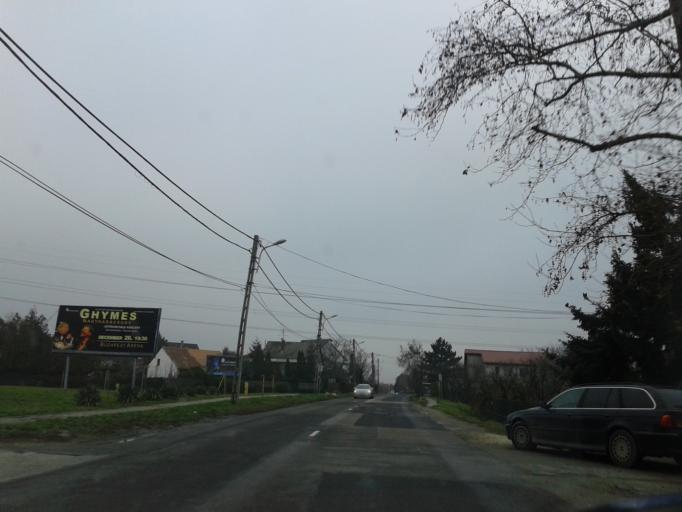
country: HU
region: Budapest
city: Budapest XXII. keruelet
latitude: 47.4297
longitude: 19.0069
